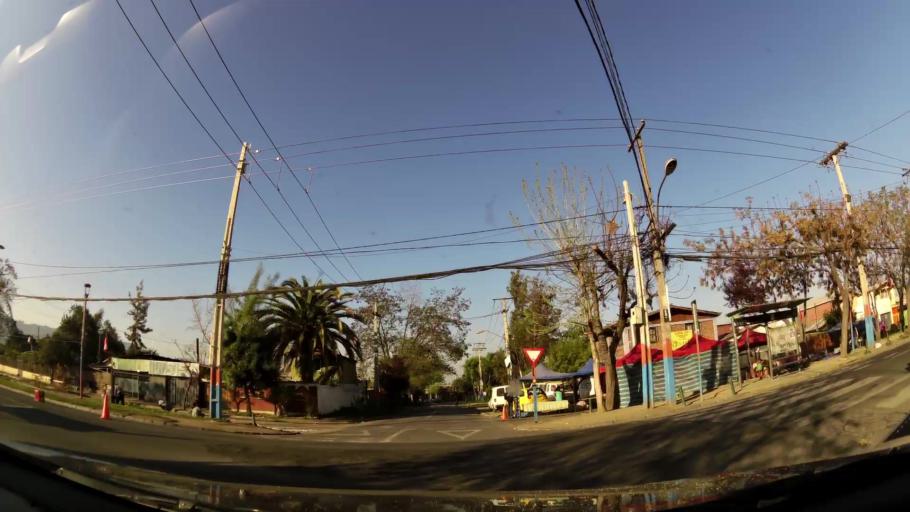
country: CL
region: Santiago Metropolitan
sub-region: Provincia de Santiago
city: Santiago
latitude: -33.3771
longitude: -70.6271
